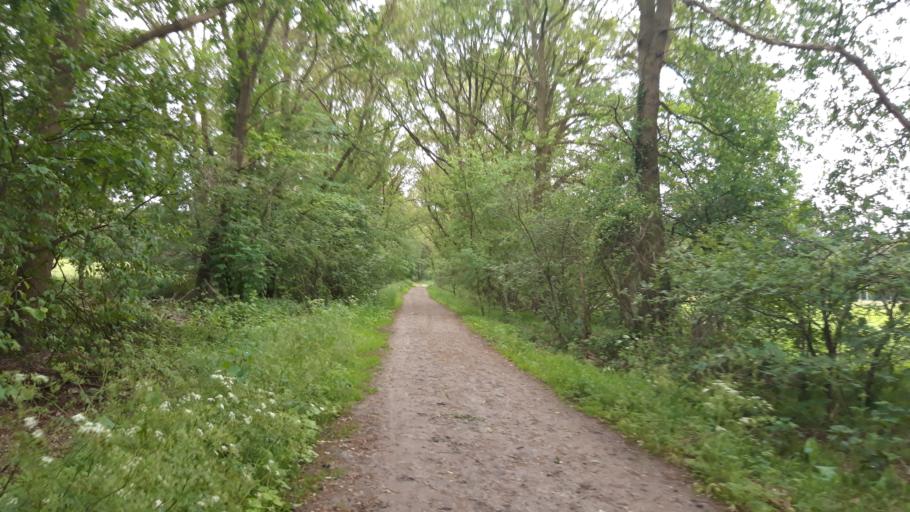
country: NL
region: Utrecht
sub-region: Gemeente Soest
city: Soest
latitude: 52.1587
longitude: 5.3210
